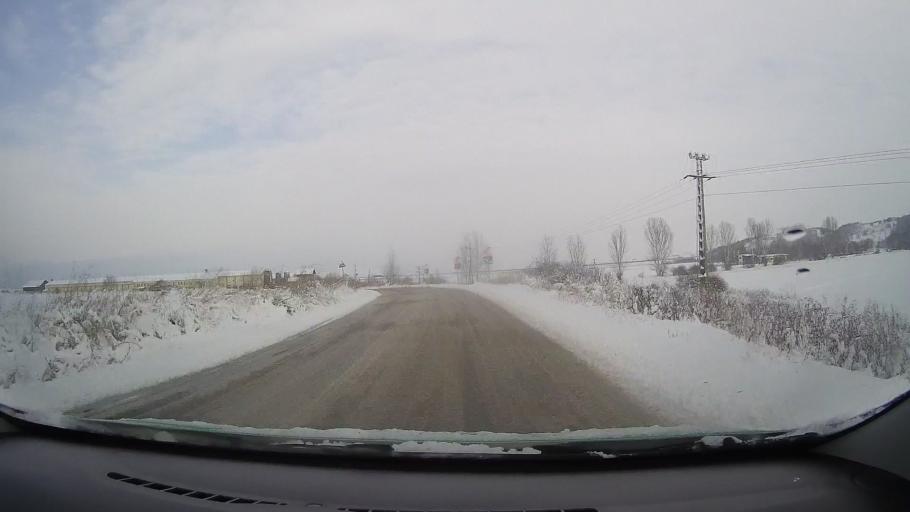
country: RO
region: Alba
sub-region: Comuna Pianu
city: Pianu de Jos
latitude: 45.9578
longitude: 23.4770
